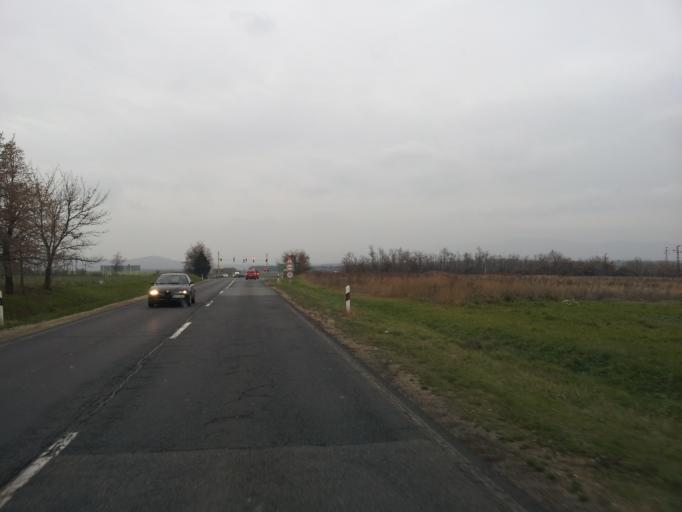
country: HU
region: Veszprem
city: Veszprem
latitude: 47.0777
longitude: 17.8950
